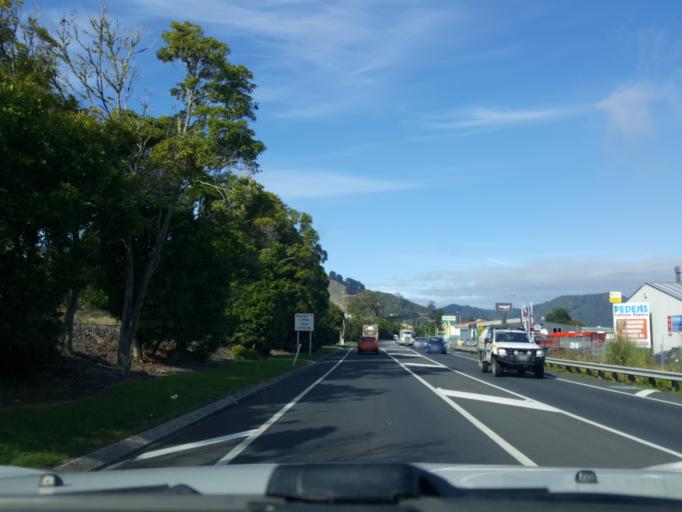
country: NZ
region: Waikato
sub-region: Waikato District
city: Ngaruawahia
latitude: -37.5711
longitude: 175.1584
